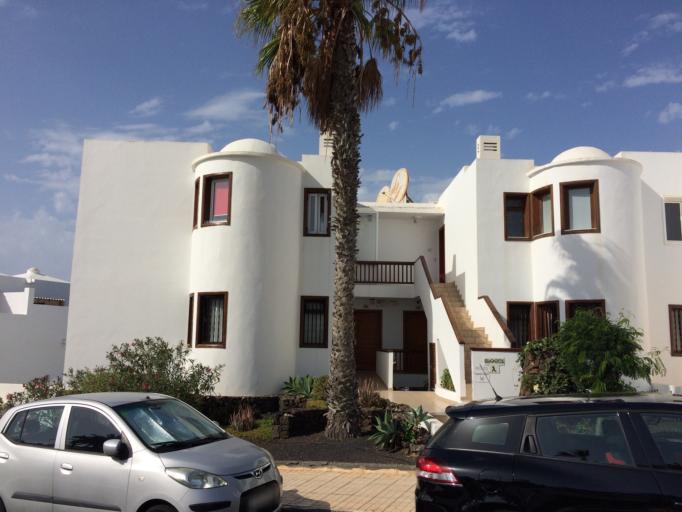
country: ES
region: Canary Islands
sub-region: Provincia de Las Palmas
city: Arrecife
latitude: 28.9945
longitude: -13.4955
